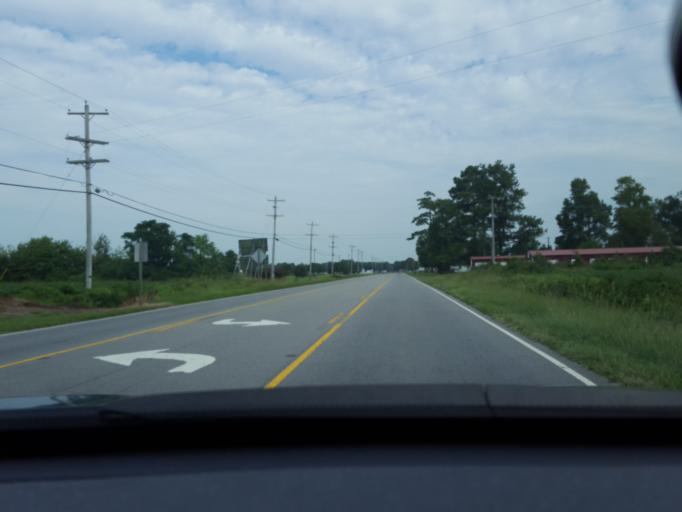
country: US
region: North Carolina
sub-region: Chowan County
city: Edenton
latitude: 36.0871
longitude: -76.6297
